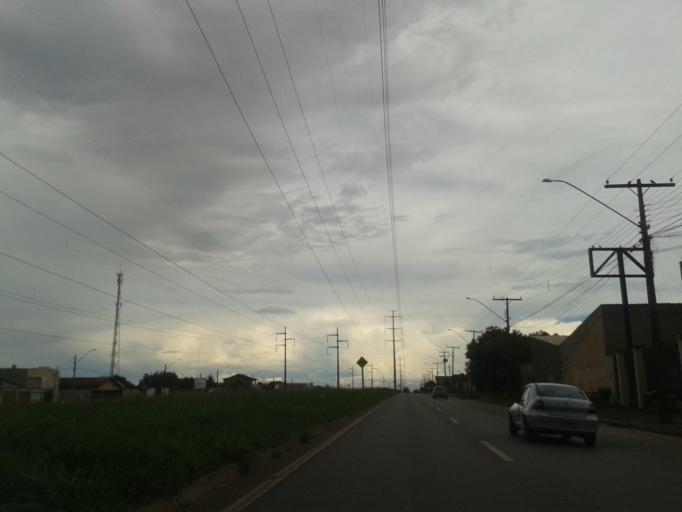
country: BR
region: Goias
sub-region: Aparecida De Goiania
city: Aparecida de Goiania
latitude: -16.7814
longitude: -49.2815
